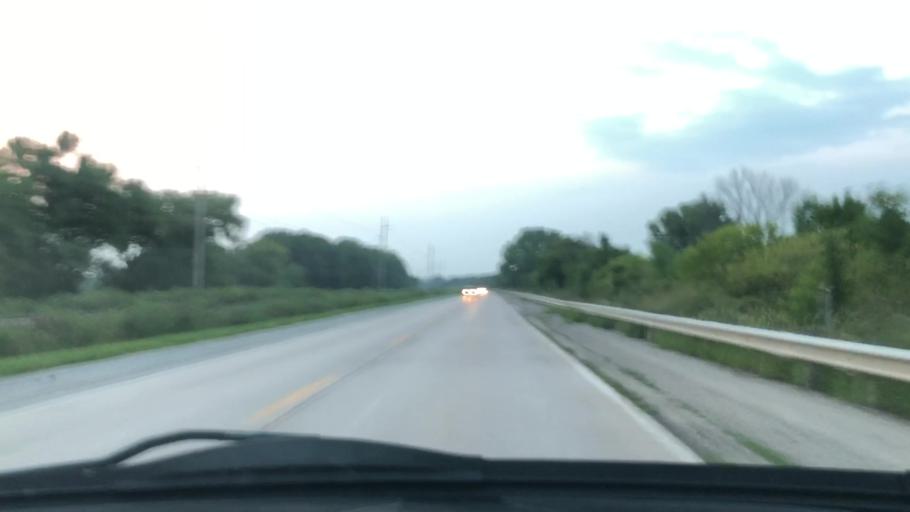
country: US
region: Iowa
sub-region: Johnson County
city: North Liberty
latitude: 41.7913
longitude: -91.6393
